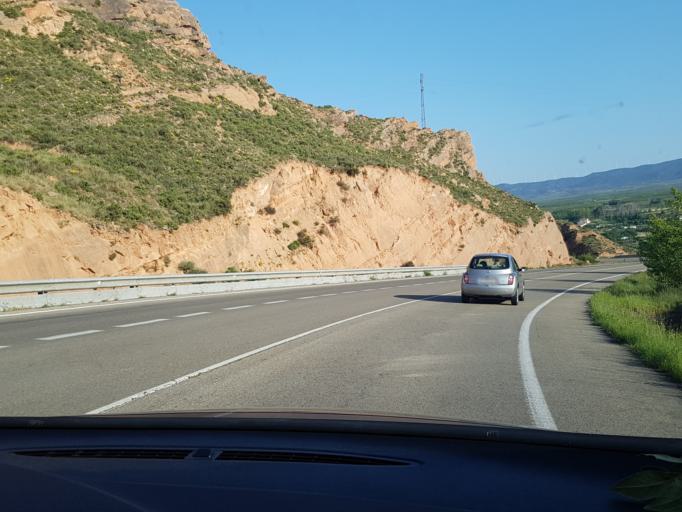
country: ES
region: La Rioja
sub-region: Provincia de La Rioja
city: Arnedo
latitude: 42.2354
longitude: -2.0820
